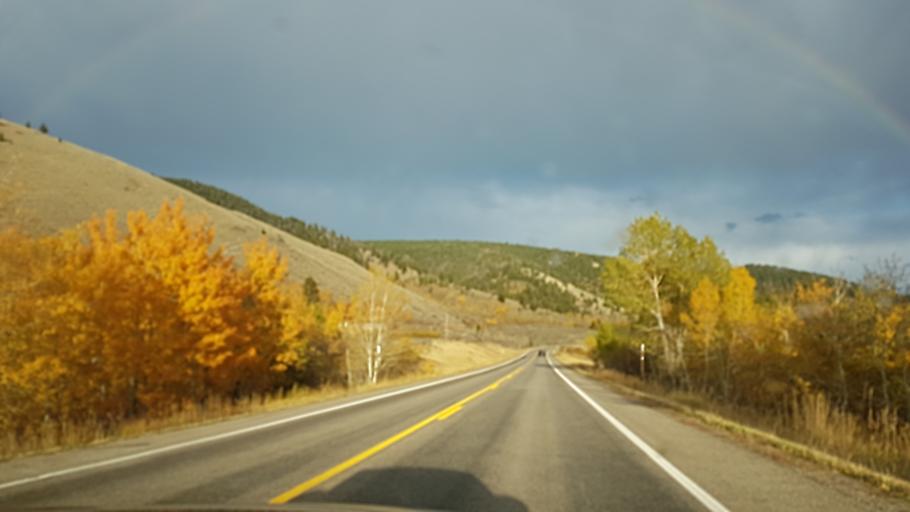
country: US
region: Montana
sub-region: Gallatin County
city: West Yellowstone
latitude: 44.6628
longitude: -111.3747
